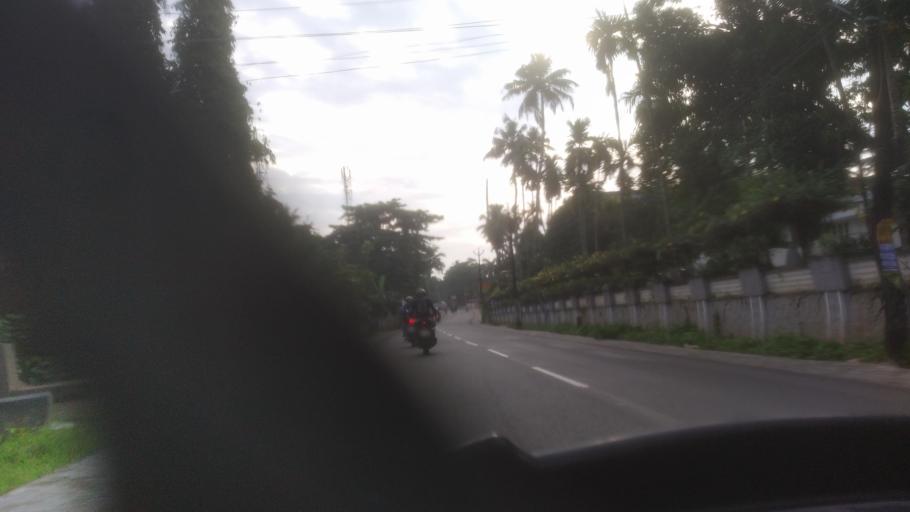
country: IN
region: Kerala
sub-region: Ernakulam
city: Kotamangalam
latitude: 10.0596
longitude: 76.6372
